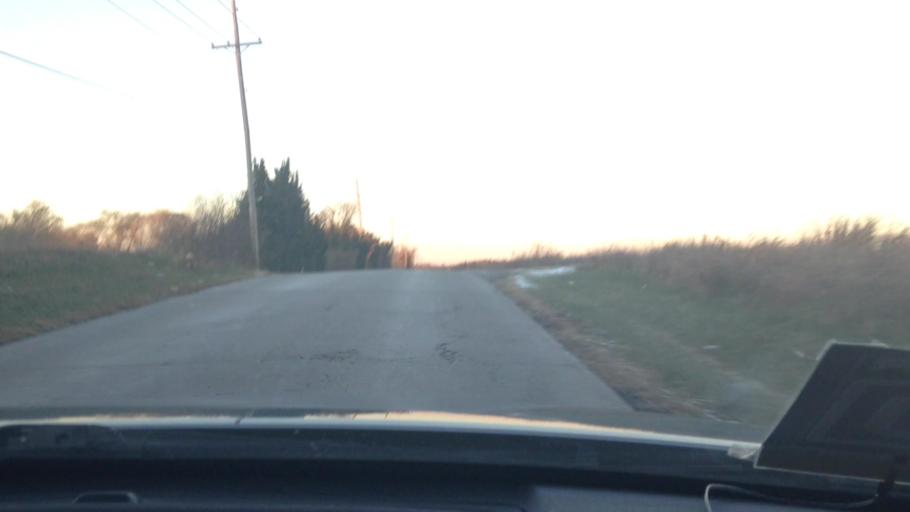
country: US
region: Kansas
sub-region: Wyandotte County
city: Bonner Springs
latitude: 39.1194
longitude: -94.8538
